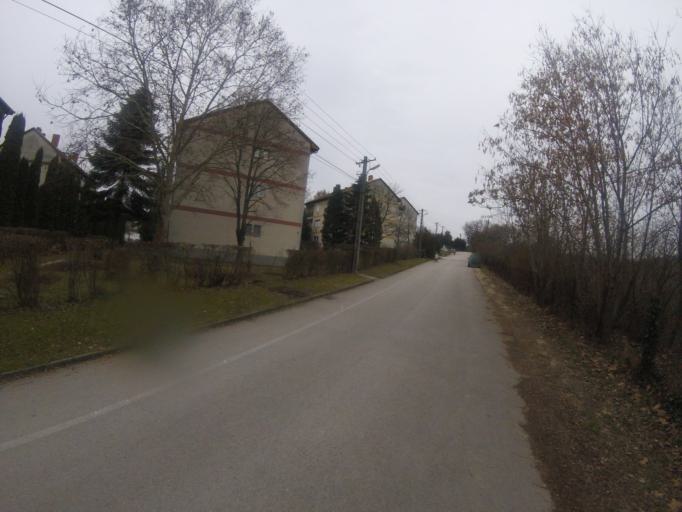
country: HU
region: Somogy
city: Balatonfoldvar
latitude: 46.8442
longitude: 17.8782
